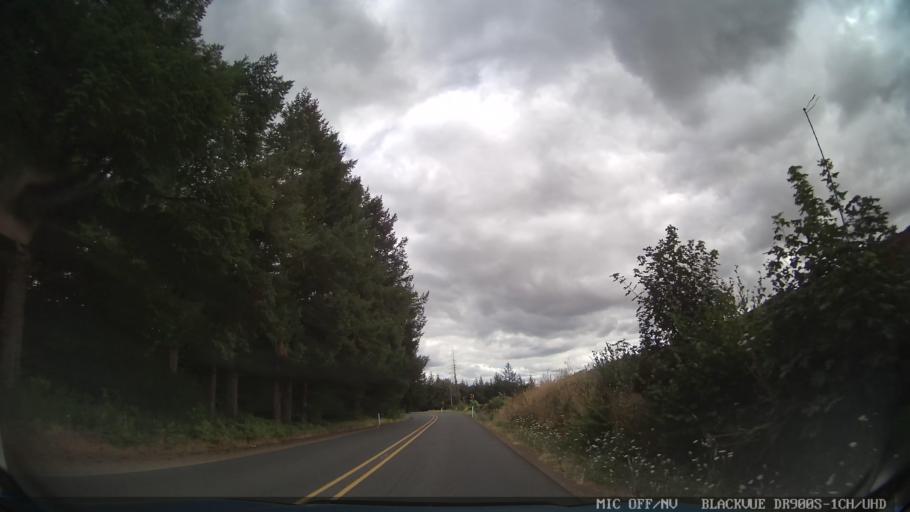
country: US
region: Oregon
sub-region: Linn County
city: Lyons
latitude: 44.8527
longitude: -122.6791
